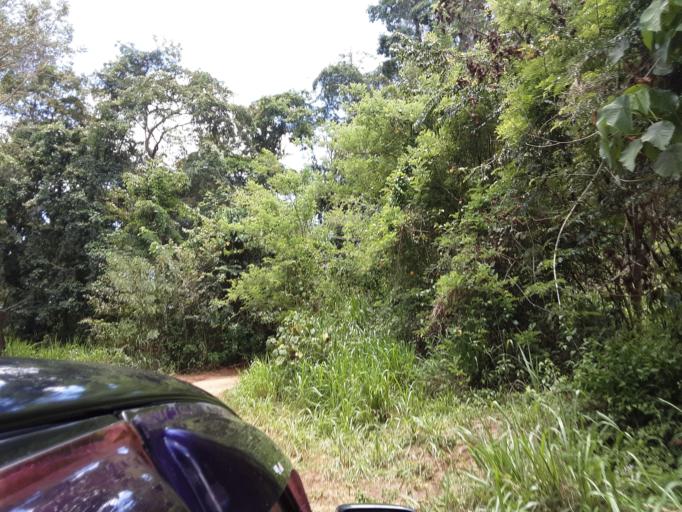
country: LK
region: Uva
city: Haputale
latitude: 6.8115
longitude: 81.1091
